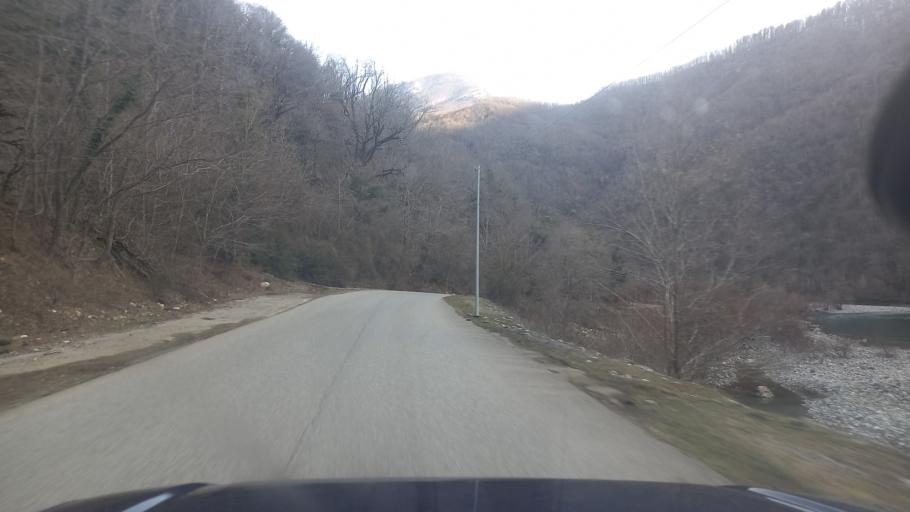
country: GE
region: Abkhazia
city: Gagra
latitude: 43.3067
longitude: 40.4070
